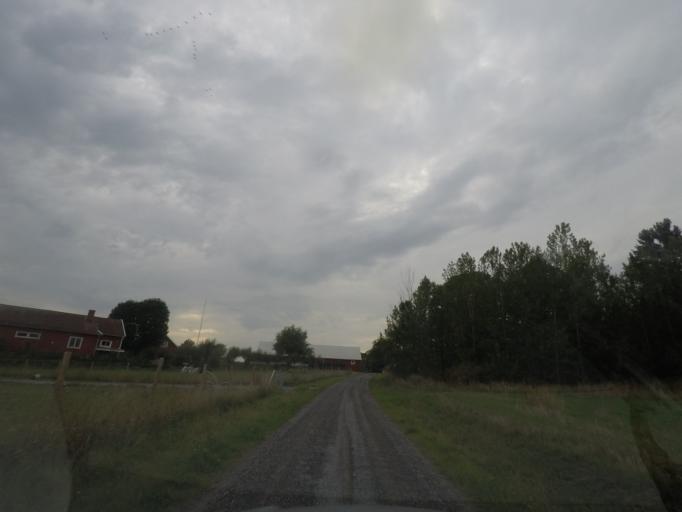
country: SE
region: Vaestmanland
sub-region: Hallstahammars Kommun
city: Kolback
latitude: 59.4794
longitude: 16.1997
